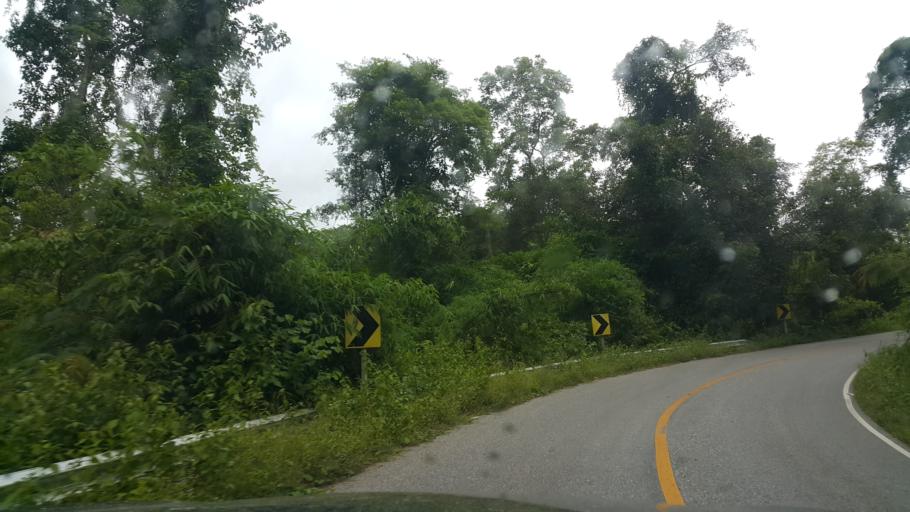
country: TH
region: Loei
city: Na Haeo
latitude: 17.5054
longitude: 100.8155
